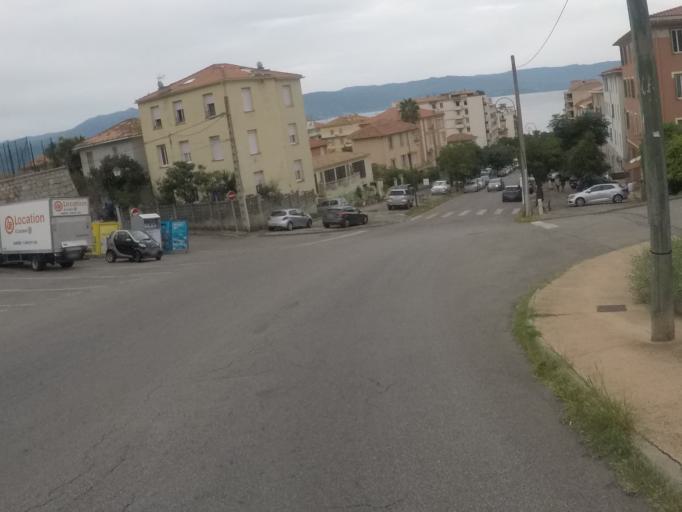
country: FR
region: Corsica
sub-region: Departement de la Corse-du-Sud
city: Ajaccio
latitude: 41.9159
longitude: 8.7238
